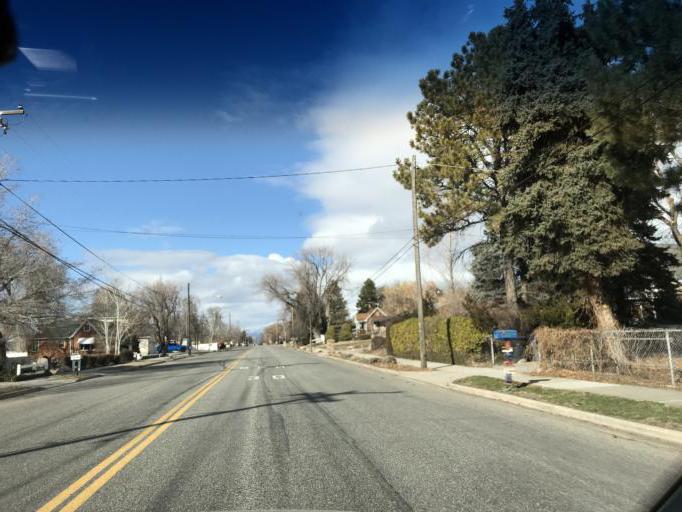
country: US
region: Utah
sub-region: Davis County
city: Woods Cross
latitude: 40.8667
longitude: -111.9020
